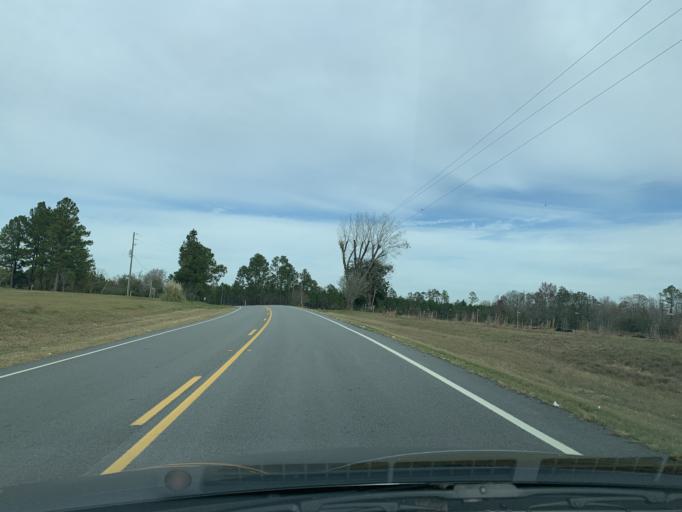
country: US
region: Georgia
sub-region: Wilcox County
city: Rochelle
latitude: 31.8433
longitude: -83.4252
